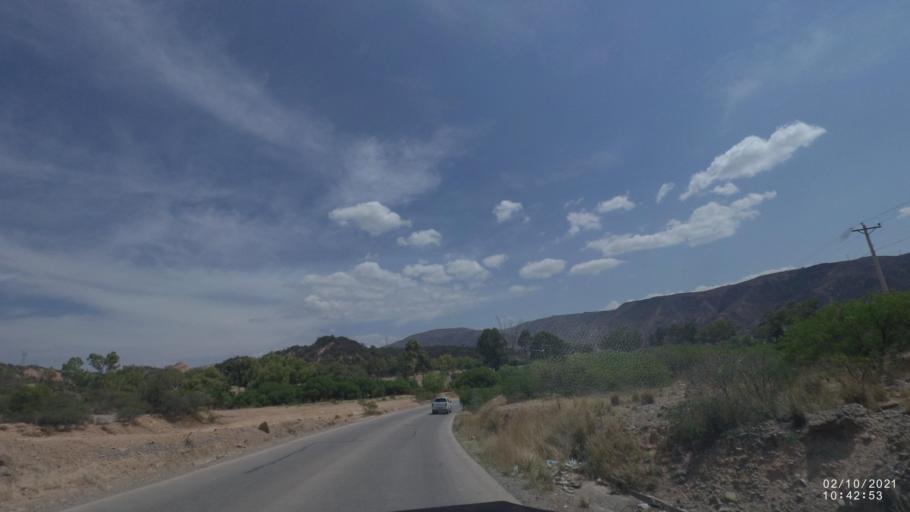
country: BO
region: Cochabamba
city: Capinota
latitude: -17.6031
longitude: -66.2972
